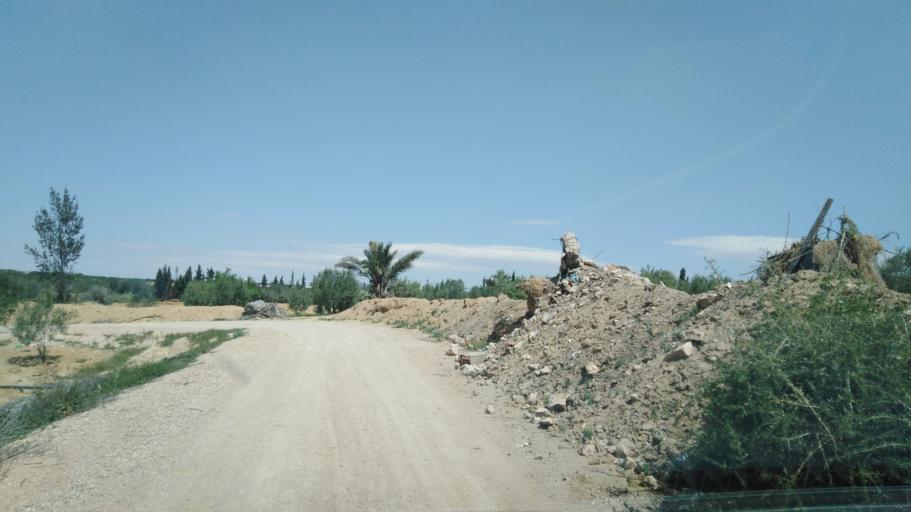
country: TN
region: Safaqis
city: Sfax
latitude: 34.7629
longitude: 10.5243
